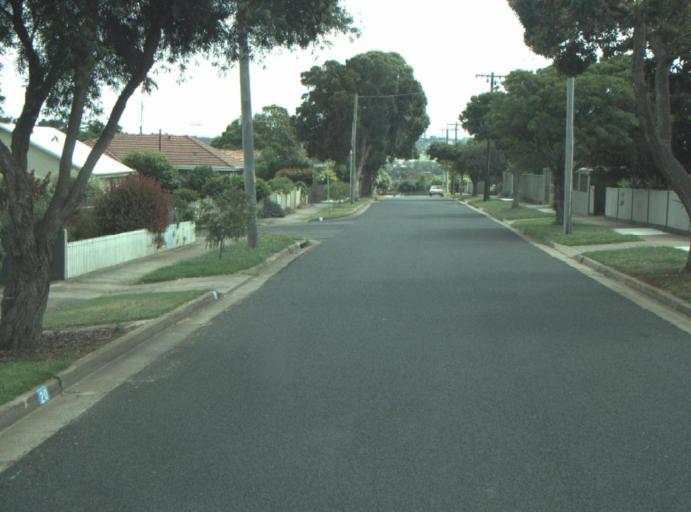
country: AU
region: Victoria
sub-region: Greater Geelong
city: Wandana Heights
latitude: -38.1754
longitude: 144.3255
